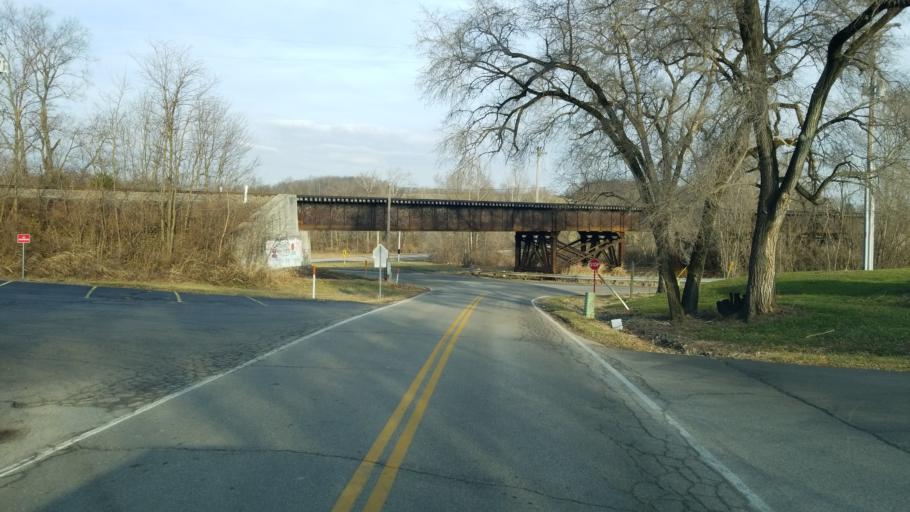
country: US
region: Ohio
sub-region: Ross County
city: Kingston
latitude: 39.4281
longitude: -82.9393
